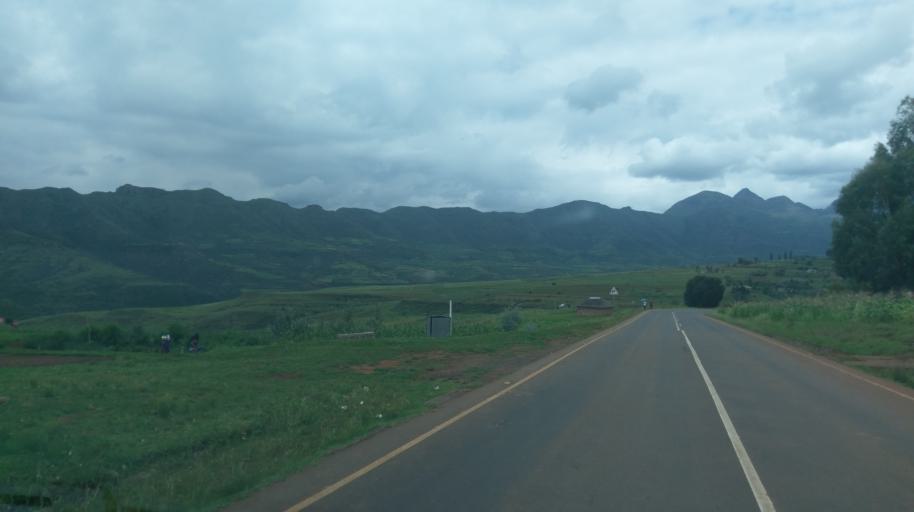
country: LS
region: Butha-Buthe
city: Butha-Buthe
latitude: -29.0335
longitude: 28.2733
